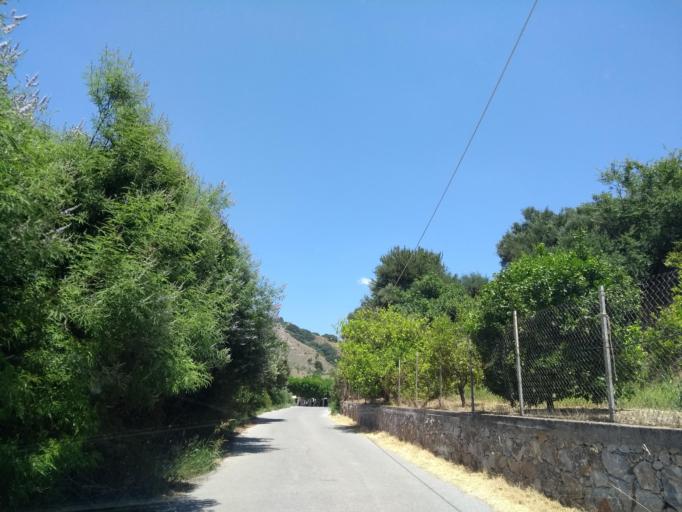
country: GR
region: Crete
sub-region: Nomos Chanias
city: Georgioupolis
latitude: 35.3339
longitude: 24.2780
